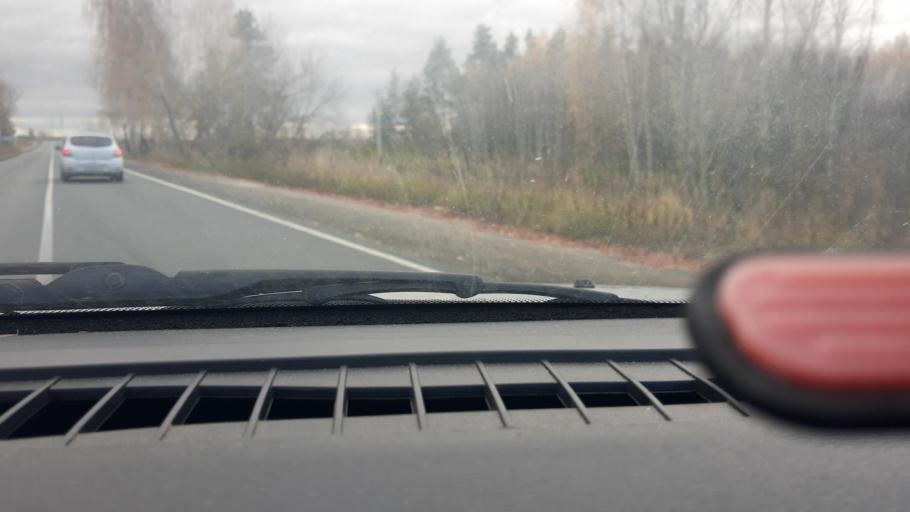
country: RU
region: Nizjnij Novgorod
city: Babino
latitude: 56.2968
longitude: 43.5972
